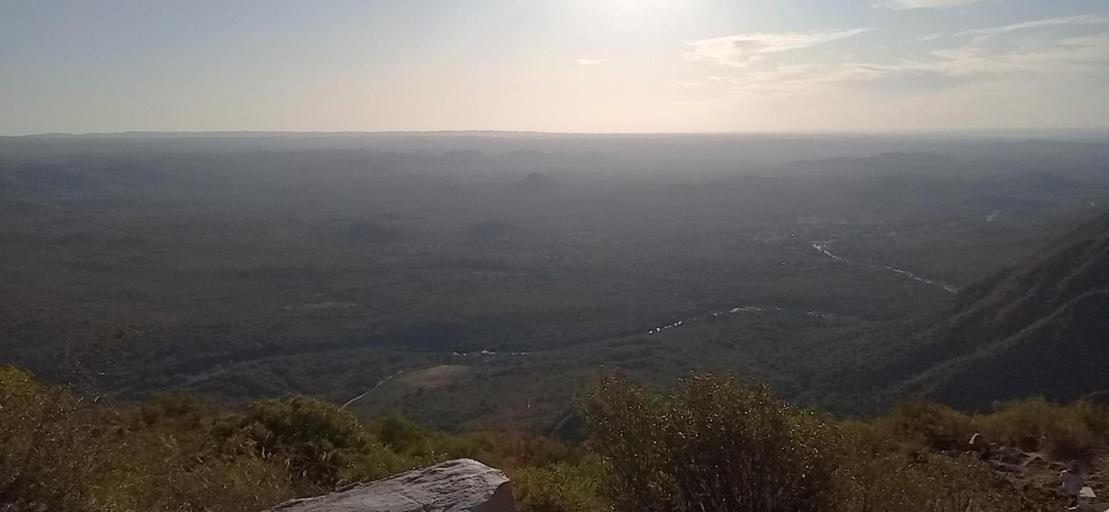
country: AR
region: Cordoba
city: Dolores
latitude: -30.9672
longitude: -64.5849
